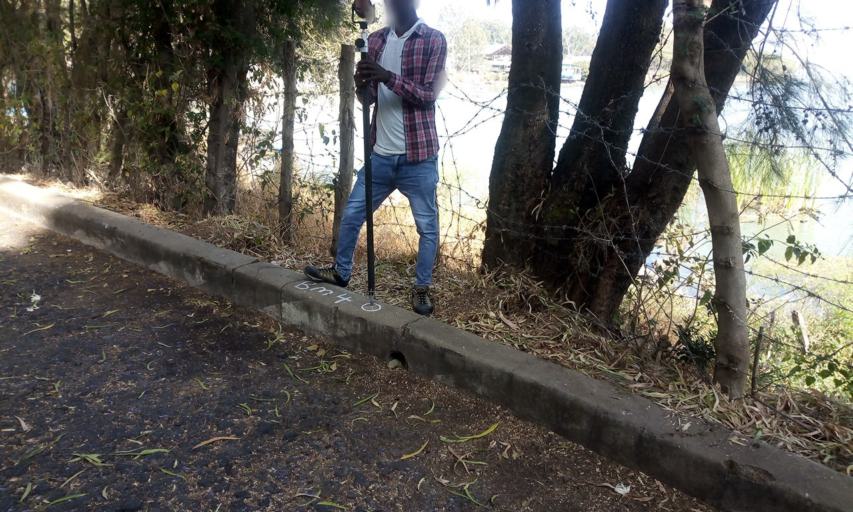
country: ET
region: Amhara
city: Gondar
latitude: 12.2392
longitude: 37.3026
